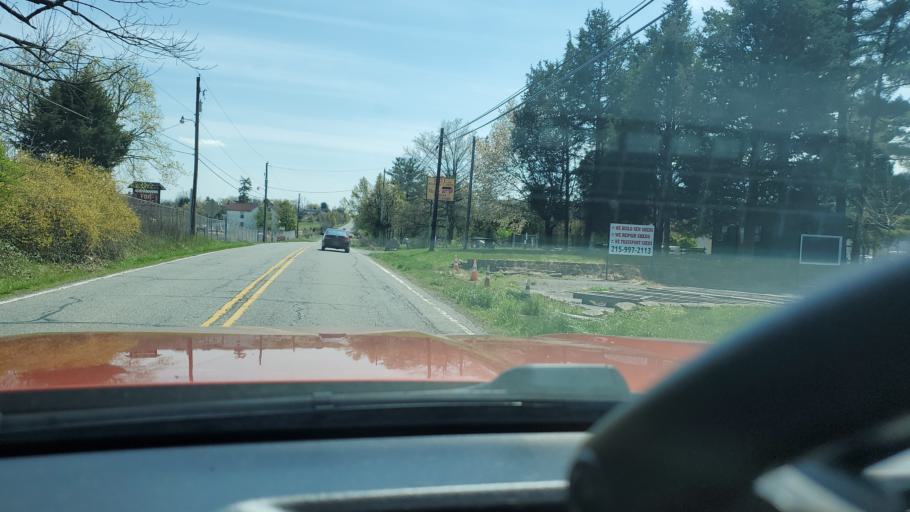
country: US
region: Pennsylvania
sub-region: Montgomery County
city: Red Hill
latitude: 40.3646
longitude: -75.4828
